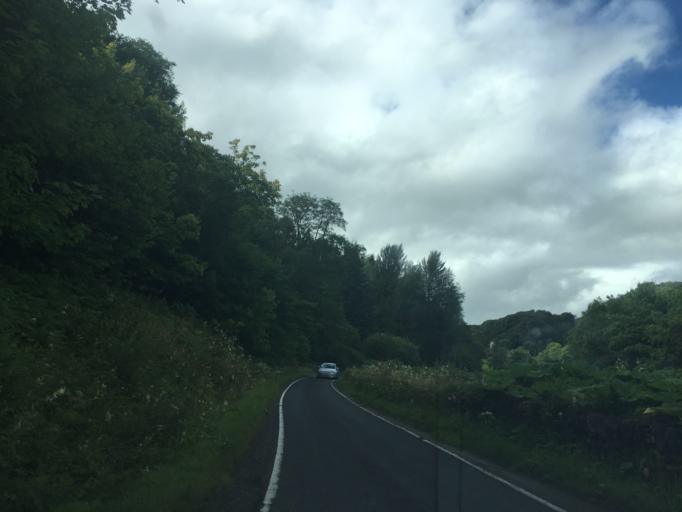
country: GB
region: Scotland
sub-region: Argyll and Bute
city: Ardrishaig
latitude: 56.0803
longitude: -5.5505
